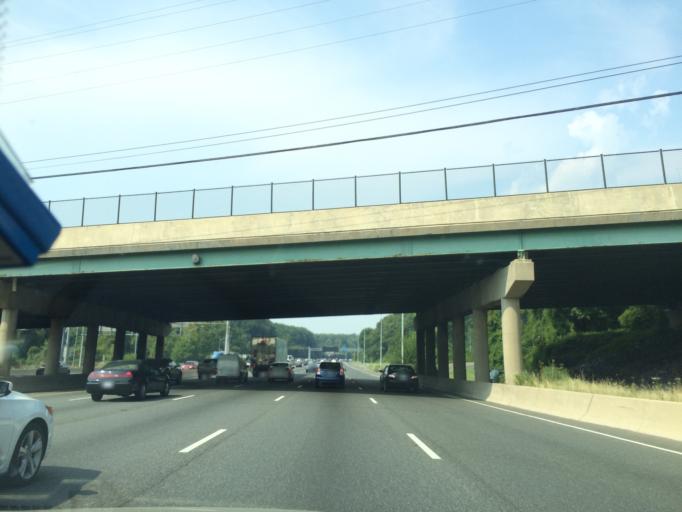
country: US
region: Maryland
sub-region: Montgomery County
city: Cabin John
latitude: 38.9906
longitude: -77.1571
